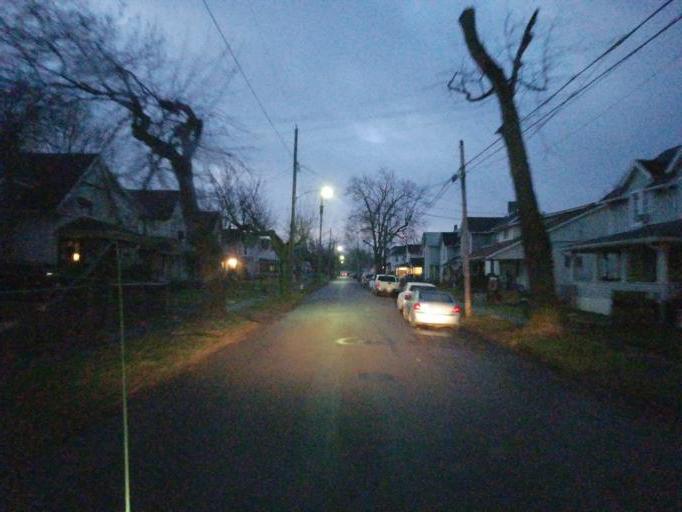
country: US
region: Ohio
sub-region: Marion County
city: Marion
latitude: 40.5795
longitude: -83.1337
